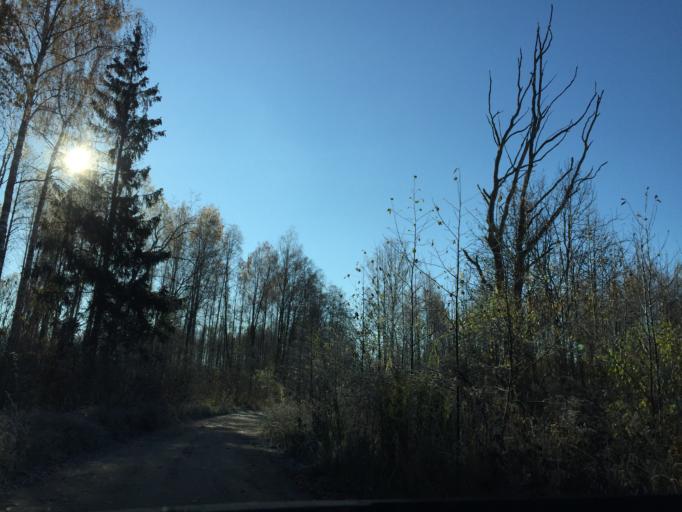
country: LV
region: Aizkraukles Rajons
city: Aizkraukle
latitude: 56.7124
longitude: 25.3006
